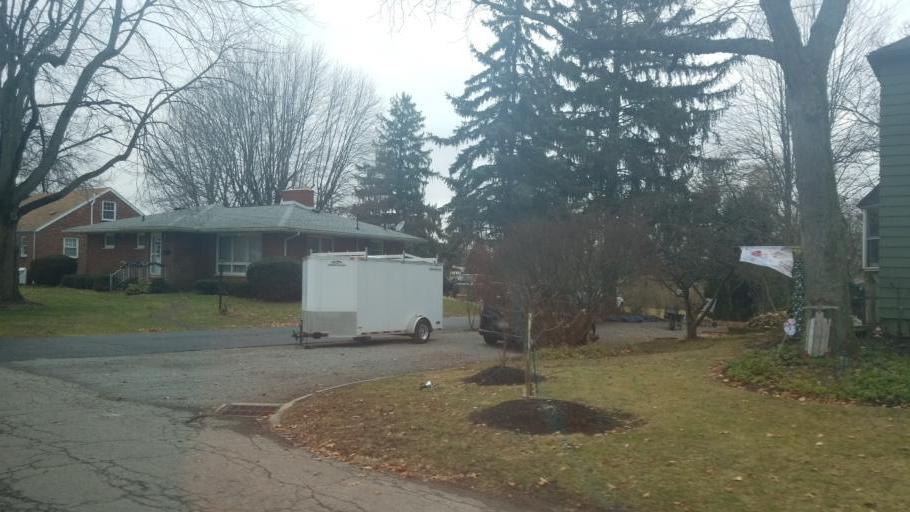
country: US
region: Ohio
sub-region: Crawford County
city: Galion
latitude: 40.7366
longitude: -82.7961
